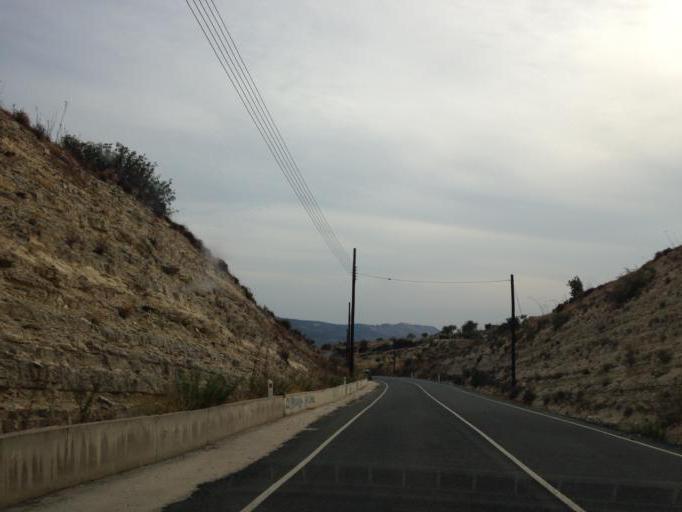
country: CY
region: Limassol
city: Pachna
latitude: 34.8224
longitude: 32.7985
